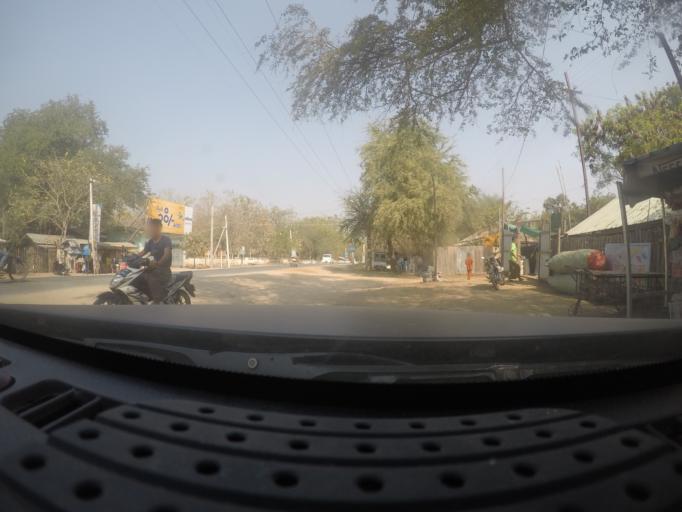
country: MM
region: Sagain
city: Sagaing
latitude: 21.9069
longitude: 95.9674
